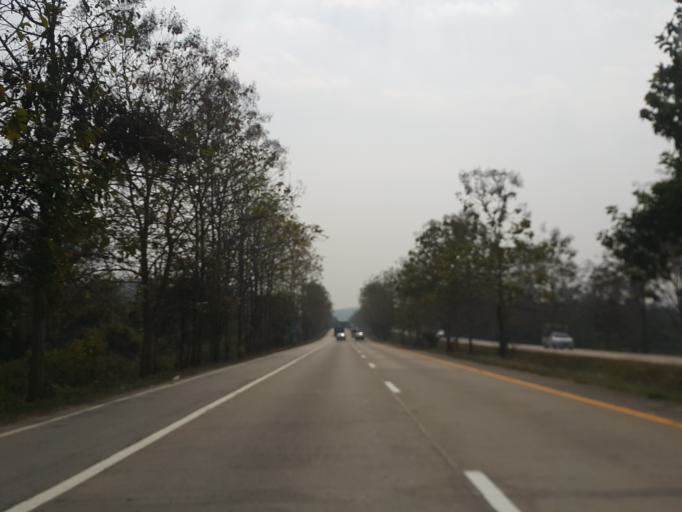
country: TH
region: Lamphun
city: Mae Tha
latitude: 18.5216
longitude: 99.0873
